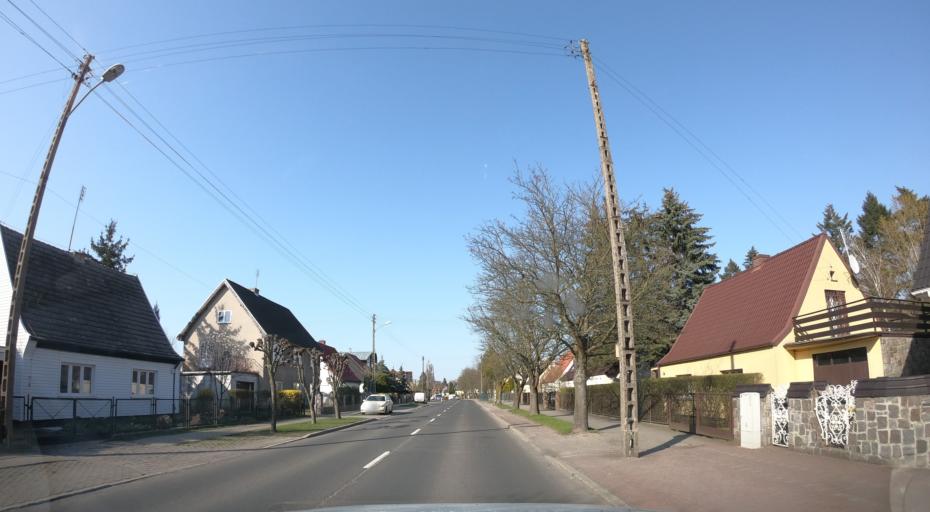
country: PL
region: West Pomeranian Voivodeship
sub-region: Powiat policki
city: Przeclaw
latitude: 53.4182
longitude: 14.4997
